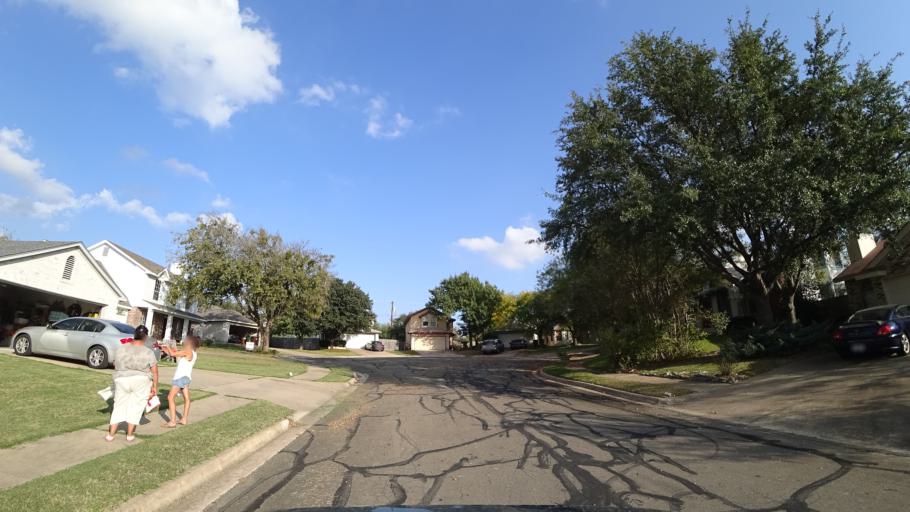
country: US
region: Texas
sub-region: Williamson County
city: Round Rock
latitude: 30.4893
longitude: -97.6568
